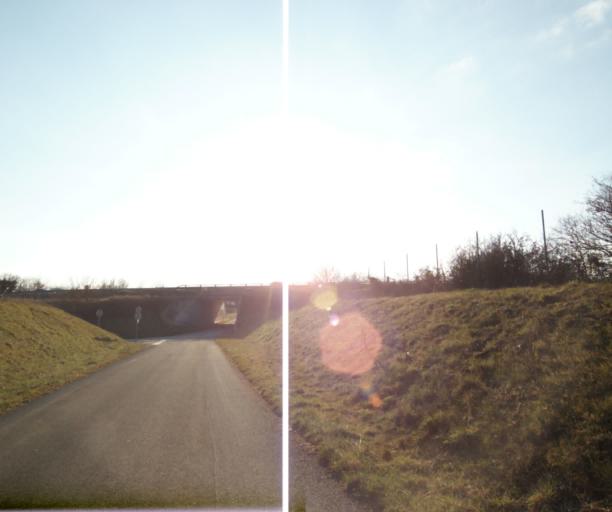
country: FR
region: Poitou-Charentes
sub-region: Departement des Deux-Sevres
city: Aiffres
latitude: 46.3279
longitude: -0.4129
